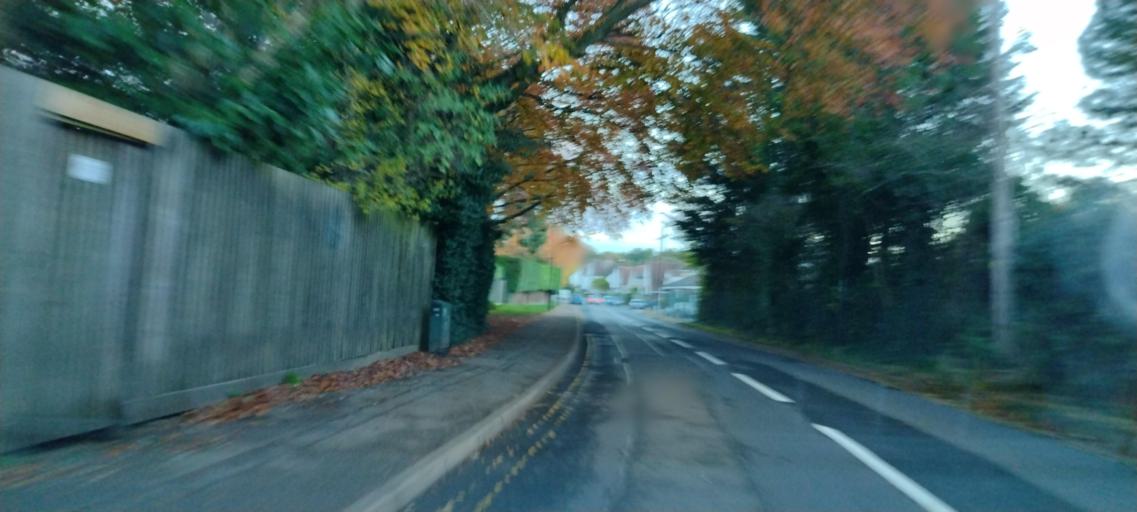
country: GB
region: England
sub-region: Coventry
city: Coventry
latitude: 52.3958
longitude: -1.5338
